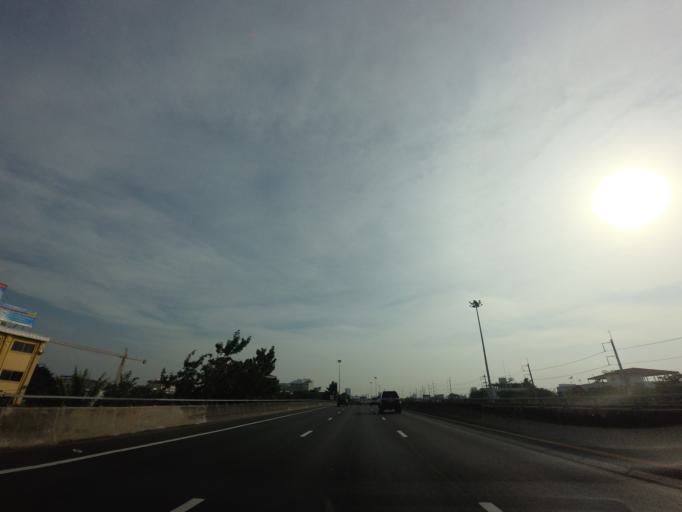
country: TH
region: Bangkok
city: Wang Thonglang
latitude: 13.7773
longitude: 100.6072
